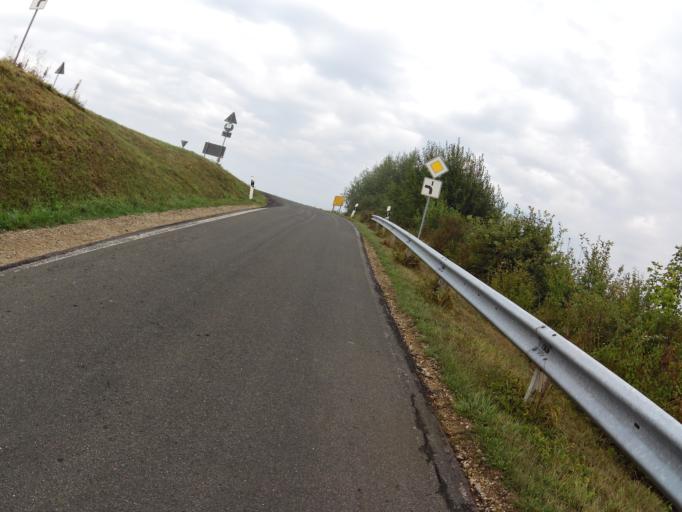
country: DE
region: Rheinland-Pfalz
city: Kyllburg
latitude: 50.0305
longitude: 6.5855
